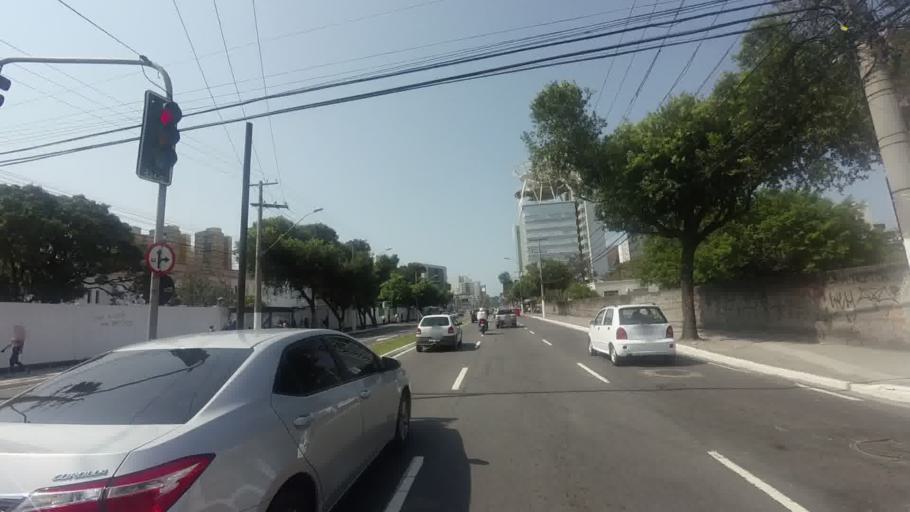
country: BR
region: Espirito Santo
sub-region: Vila Velha
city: Vila Velha
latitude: -20.2922
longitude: -40.3025
